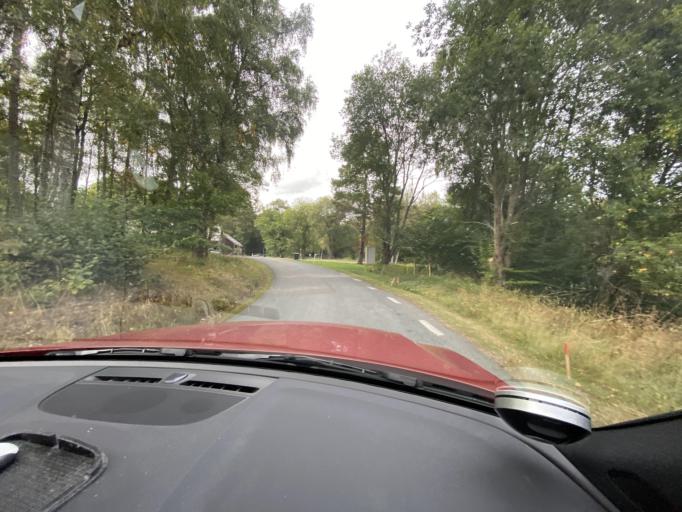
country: SE
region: Skane
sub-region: Hassleholms Kommun
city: Bjarnum
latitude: 56.3541
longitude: 13.7023
